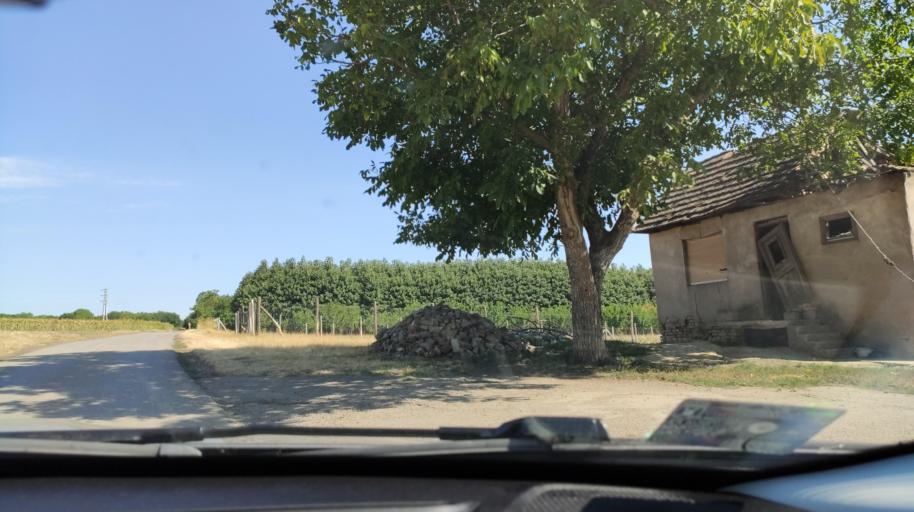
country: RS
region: Autonomna Pokrajina Vojvodina
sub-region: Severnobacki Okrug
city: Backa Topola
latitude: 45.8261
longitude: 19.6266
